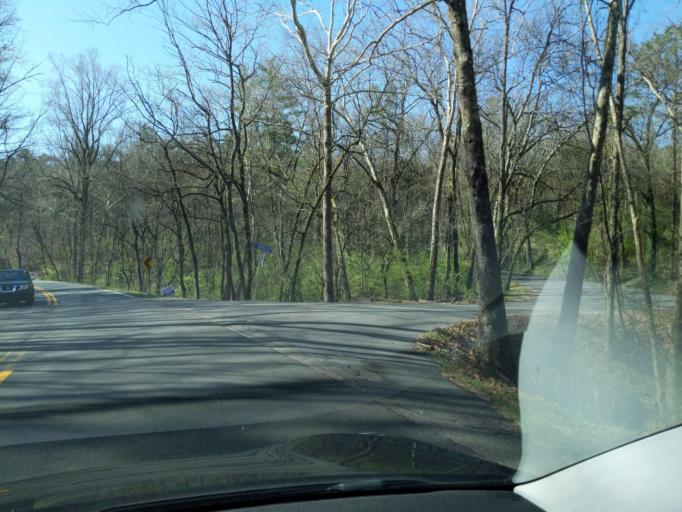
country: US
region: Tennessee
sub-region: Sevier County
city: Sevierville
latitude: 35.9621
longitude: -83.5497
